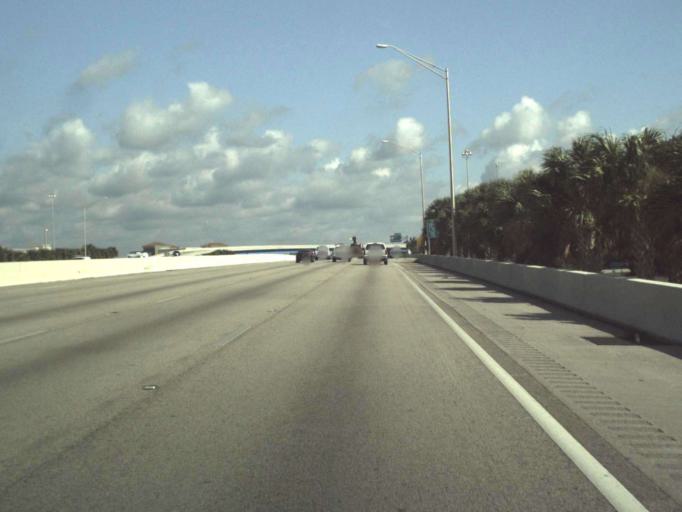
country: US
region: Florida
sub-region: Palm Beach County
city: North Palm Beach
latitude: 26.8375
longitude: -80.1002
